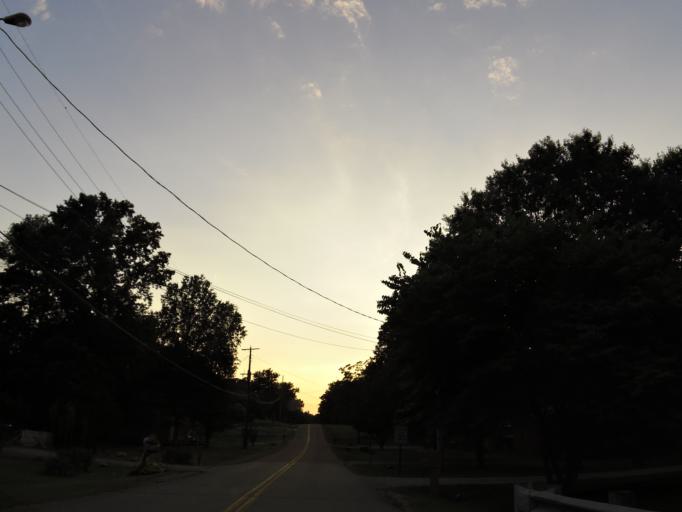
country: US
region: Tennessee
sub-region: Henry County
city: Paris
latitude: 36.2992
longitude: -88.3040
